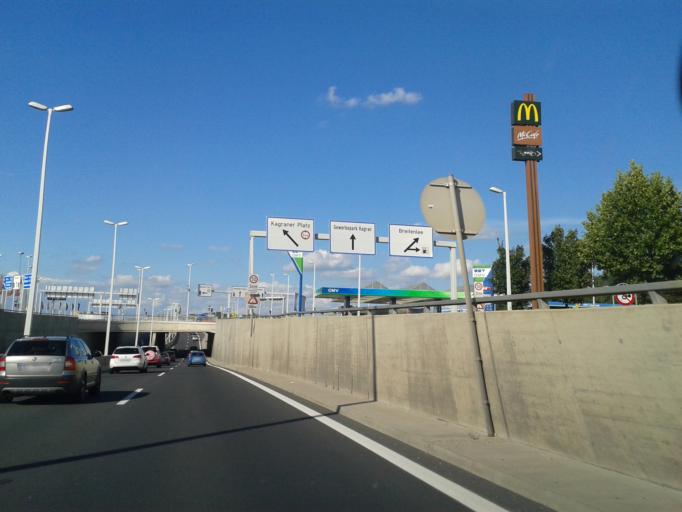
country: AT
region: Lower Austria
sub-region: Politischer Bezirk Wien-Umgebung
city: Gerasdorf bei Wien
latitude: 48.2506
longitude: 16.4706
